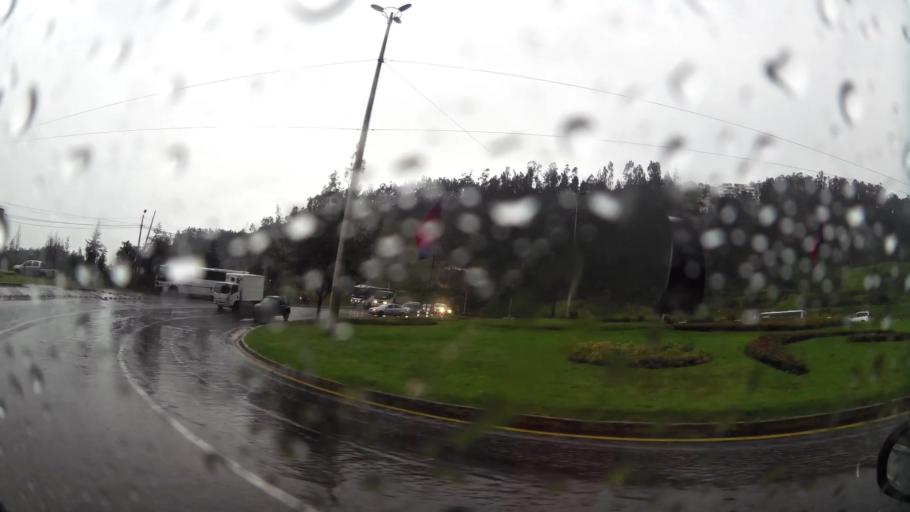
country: EC
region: Pichincha
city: Quito
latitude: -0.1501
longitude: -78.4524
